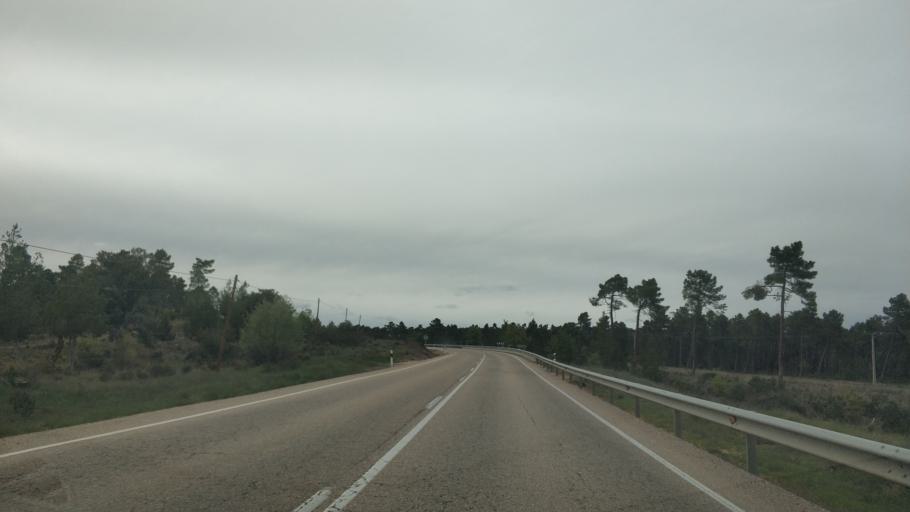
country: ES
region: Castille and Leon
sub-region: Provincia de Soria
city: Bayubas de Abajo
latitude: 41.5176
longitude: -2.9294
